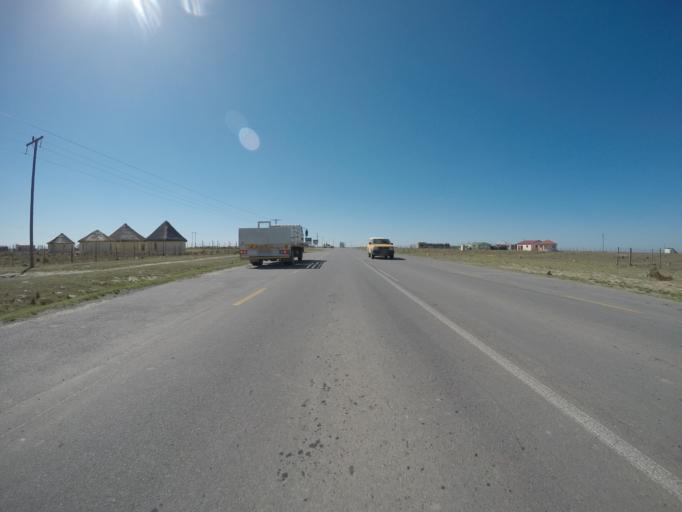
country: ZA
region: Eastern Cape
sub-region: OR Tambo District Municipality
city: Mthatha
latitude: -31.8939
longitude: 28.7820
